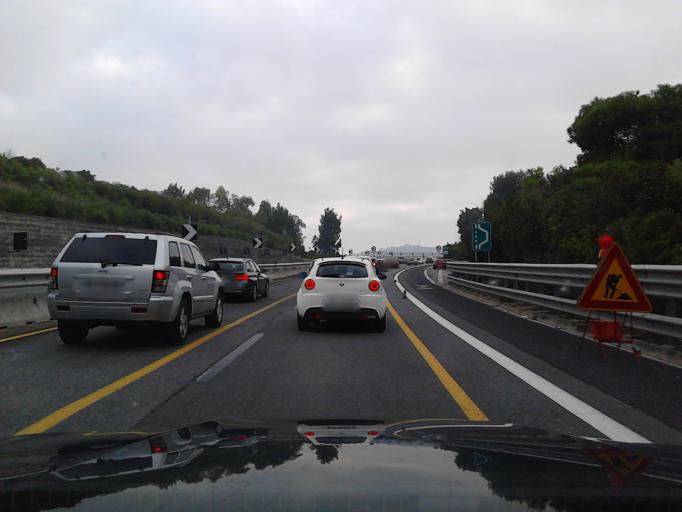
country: IT
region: Abruzzo
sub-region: Provincia di Teramo
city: Tortoreto Lido
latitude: 42.7862
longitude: 13.9355
